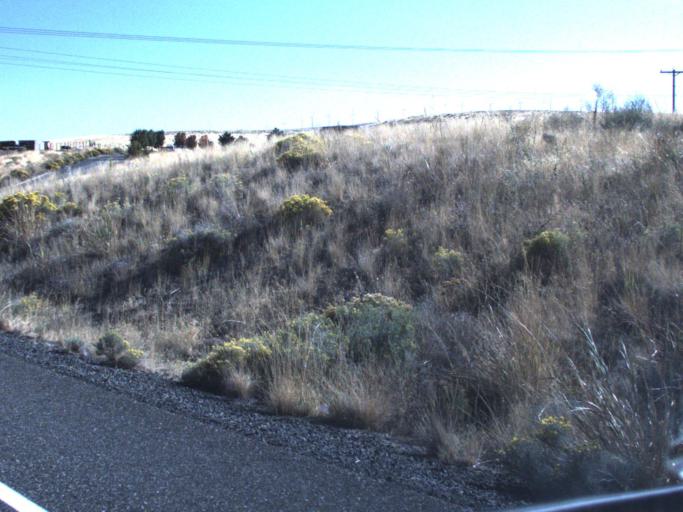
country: US
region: Washington
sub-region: Benton County
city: Highland
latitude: 46.1466
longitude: -119.1172
